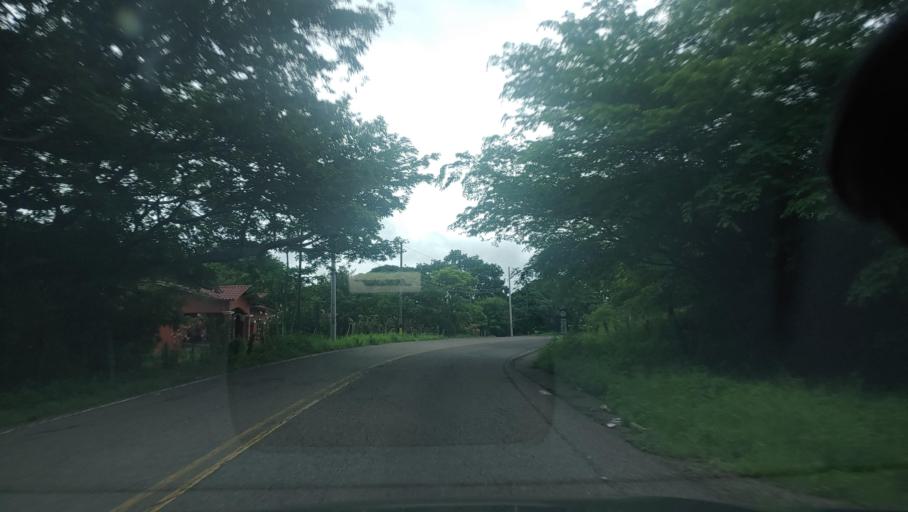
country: HN
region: Choluteca
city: Corpus
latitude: 13.3745
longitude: -87.0473
